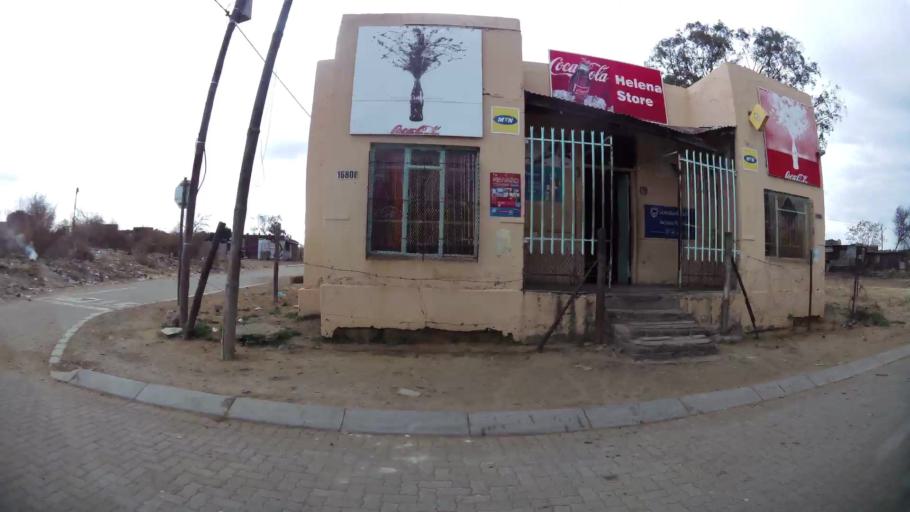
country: ZA
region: Orange Free State
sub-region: Fezile Dabi District Municipality
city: Kroonstad
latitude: -27.6467
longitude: 27.2173
